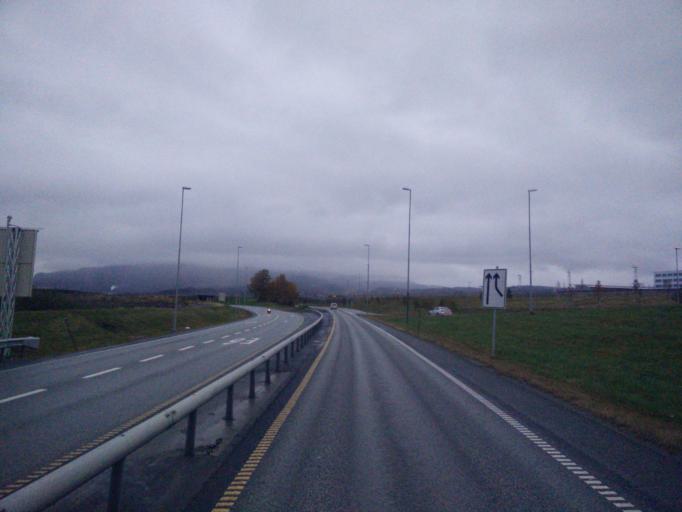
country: NO
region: Nord-Trondelag
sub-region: Stjordal
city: Stjordal
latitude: 63.4520
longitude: 10.9091
